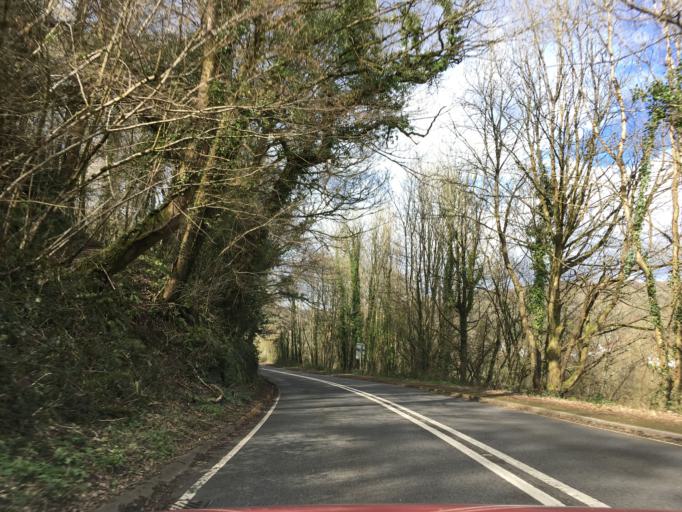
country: GB
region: Wales
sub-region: Monmouthshire
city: Tintern
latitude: 51.7072
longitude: -2.6704
